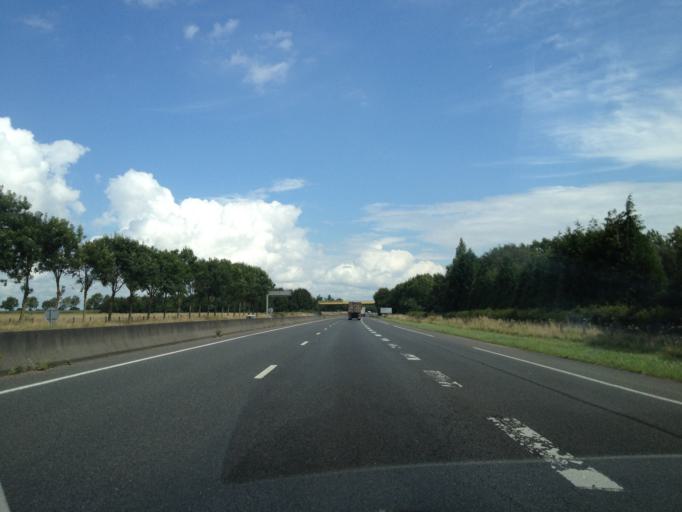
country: FR
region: Picardie
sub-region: Departement de la Somme
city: Oisemont
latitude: 50.0453
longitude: 1.7624
